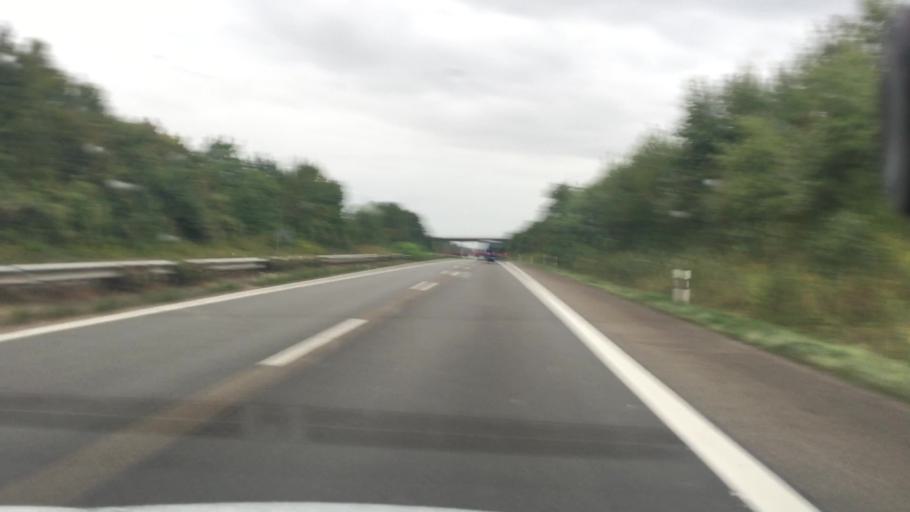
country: DE
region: Rheinland-Pfalz
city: Knoringen
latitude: 49.2427
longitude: 8.1488
